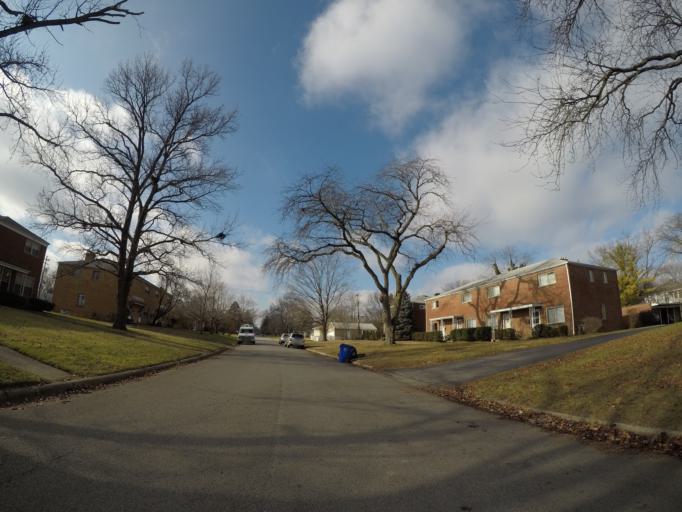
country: US
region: Ohio
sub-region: Franklin County
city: Upper Arlington
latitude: 40.0208
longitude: -83.0626
